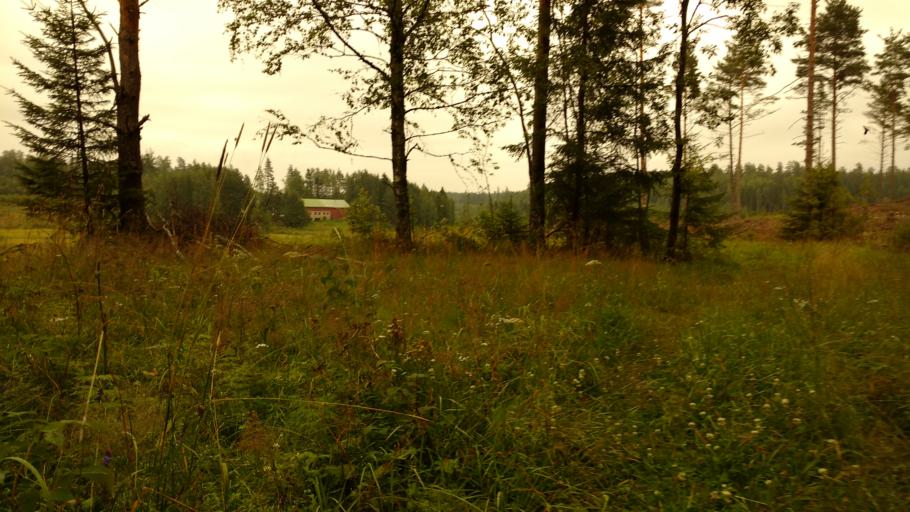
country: FI
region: Varsinais-Suomi
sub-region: Salo
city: Pertteli
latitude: 60.3993
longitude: 23.2253
